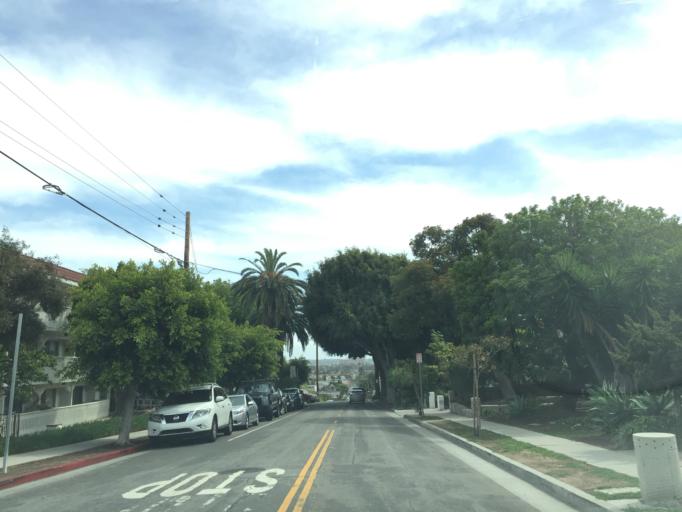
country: US
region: California
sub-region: Los Angeles County
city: Santa Monica
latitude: 33.9998
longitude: -118.4773
